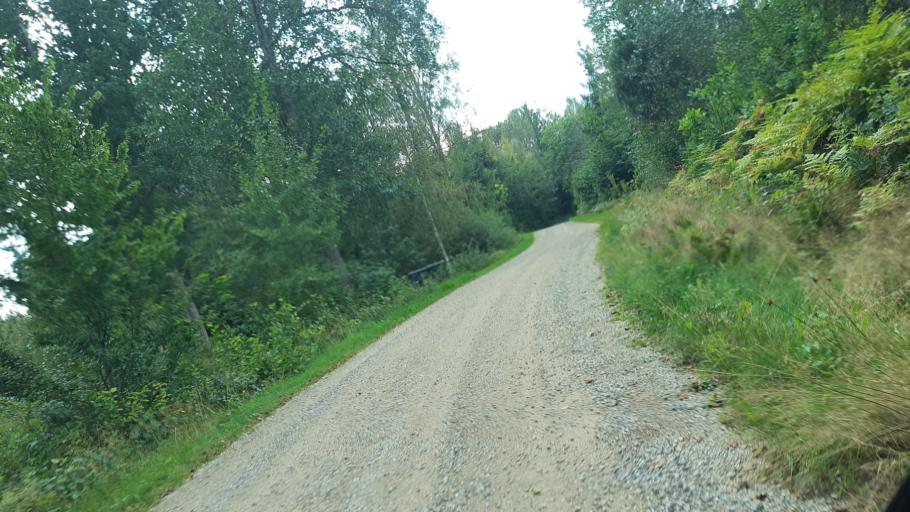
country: SE
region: Blekinge
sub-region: Ronneby Kommun
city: Brakne-Hoby
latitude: 56.4232
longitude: 15.1890
